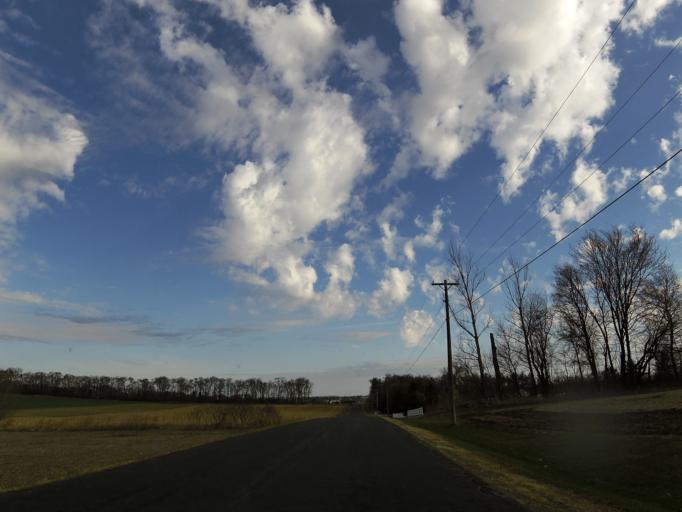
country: US
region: Minnesota
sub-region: Dakota County
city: Hastings
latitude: 44.7822
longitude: -92.8428
